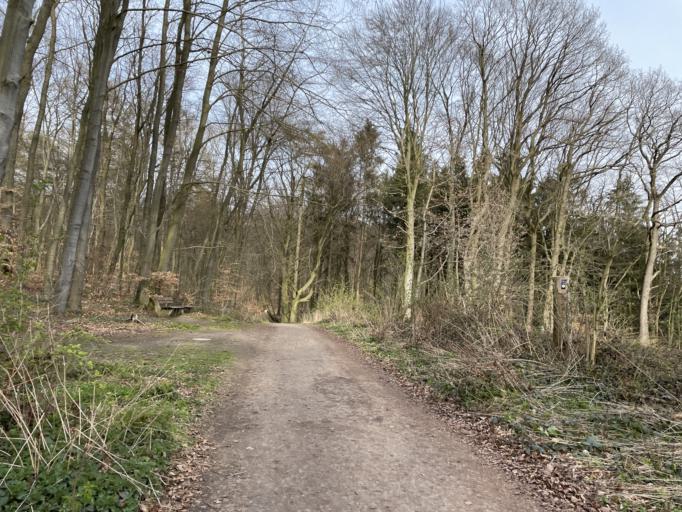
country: DE
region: North Rhine-Westphalia
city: Porta Westfalica
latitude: 52.2380
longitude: 8.9532
